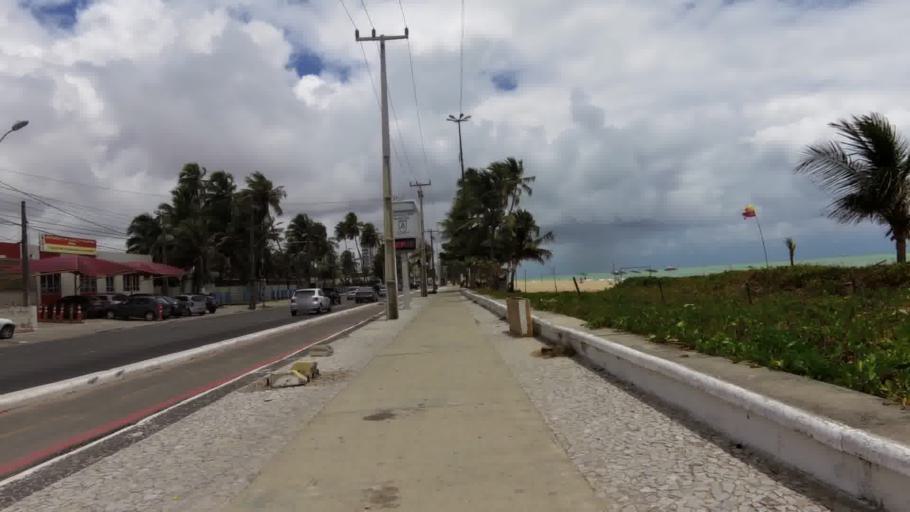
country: BR
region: Pernambuco
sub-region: Jaboatao Dos Guararapes
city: Jaboatao
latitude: -8.1594
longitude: -34.9111
